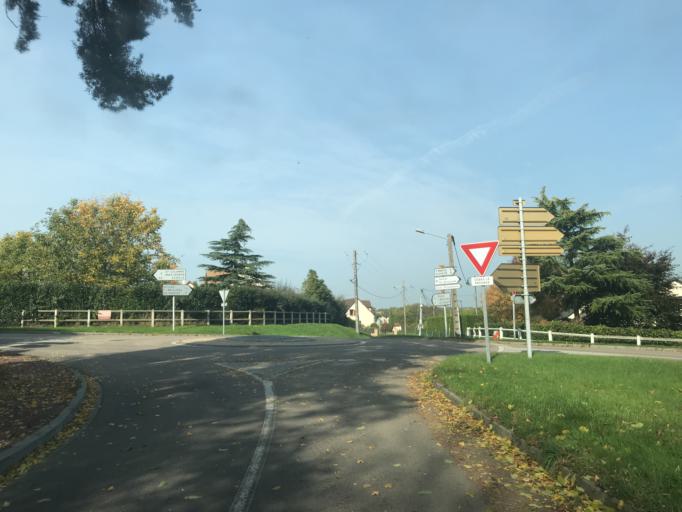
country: FR
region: Haute-Normandie
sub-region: Departement de l'Eure
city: La Chapelle-Reanville
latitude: 49.0966
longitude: 1.3742
